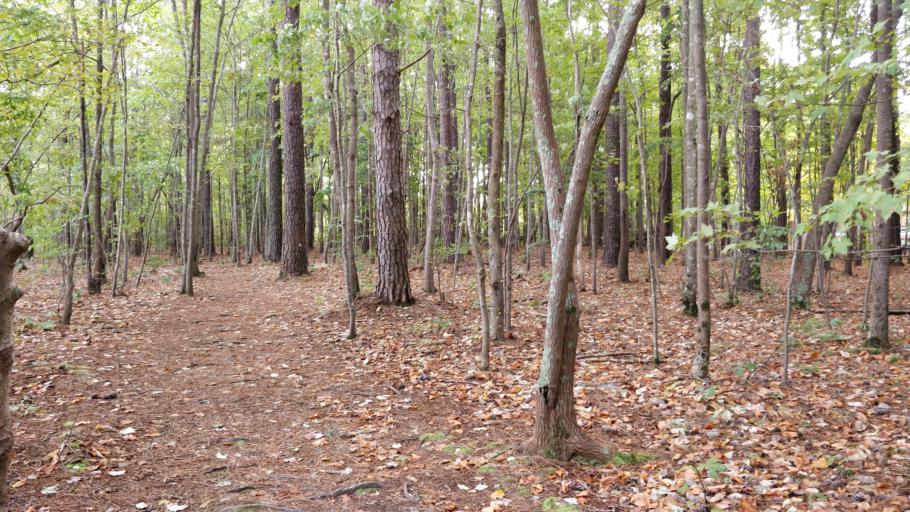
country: US
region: North Carolina
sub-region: Wake County
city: West Raleigh
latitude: 35.9060
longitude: -78.6705
